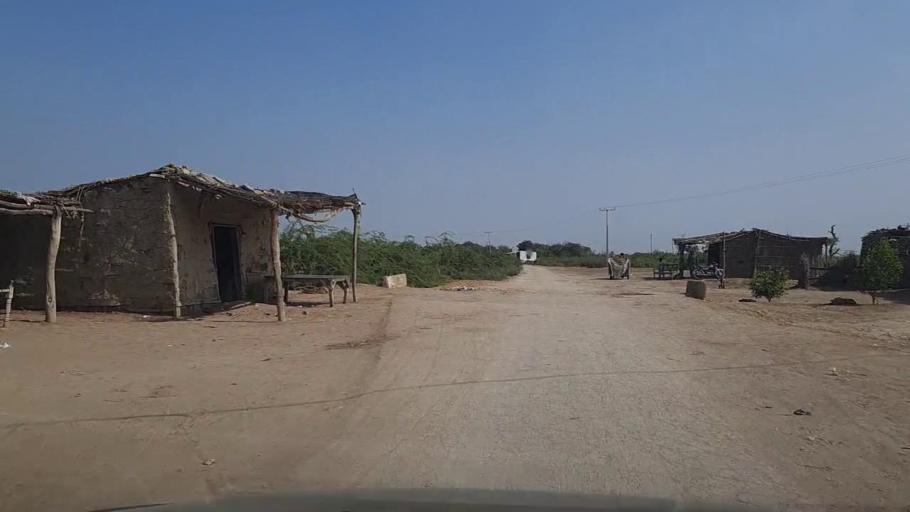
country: PK
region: Sindh
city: Thatta
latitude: 24.5928
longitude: 67.9472
